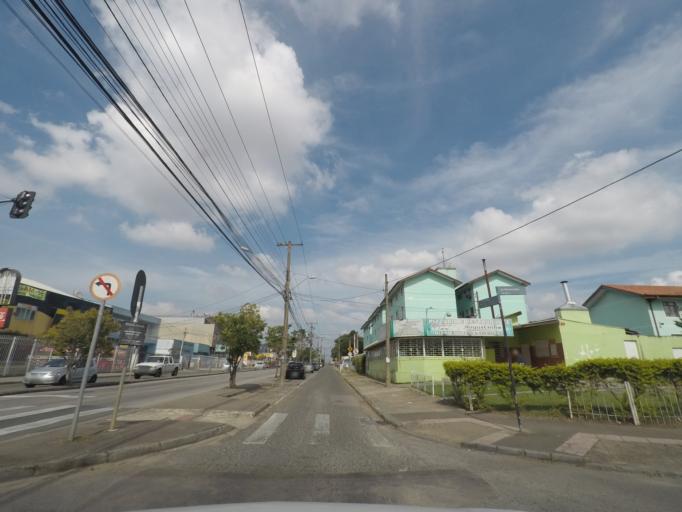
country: BR
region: Parana
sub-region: Pinhais
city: Pinhais
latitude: -25.4590
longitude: -49.2124
